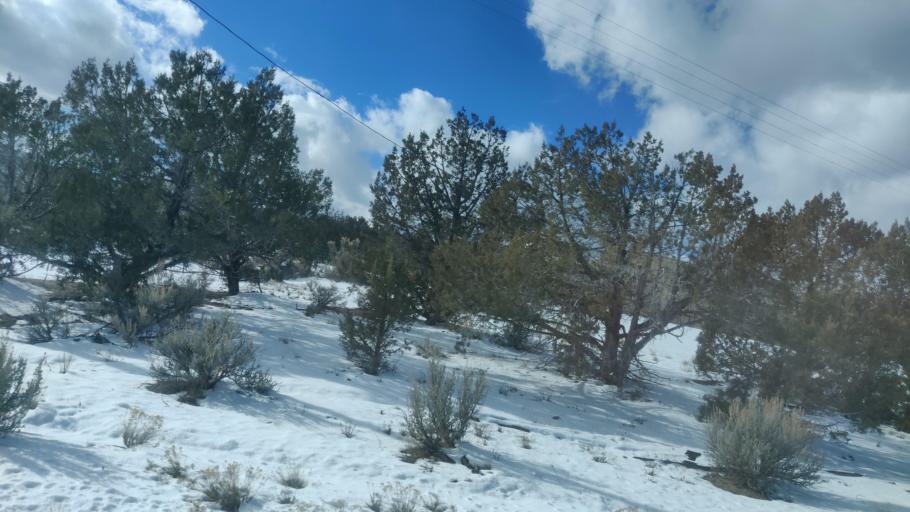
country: US
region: Colorado
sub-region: Mesa County
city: Palisade
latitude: 39.2105
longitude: -108.1475
